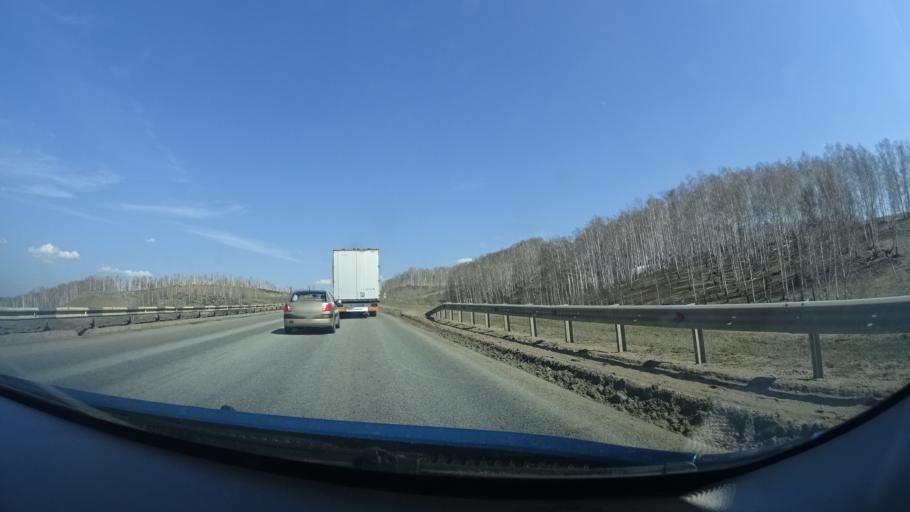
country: RU
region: Bashkortostan
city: Kandry
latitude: 54.5813
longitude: 54.2467
